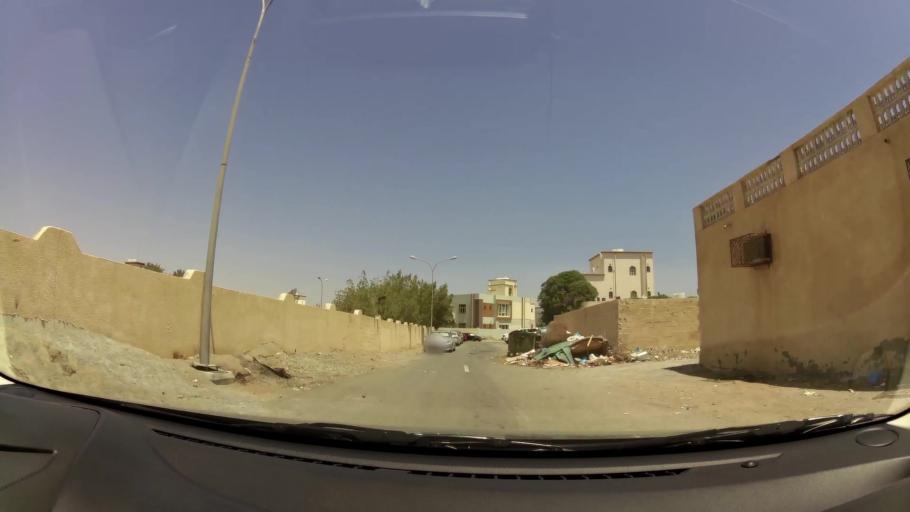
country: OM
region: Muhafazat Masqat
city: As Sib al Jadidah
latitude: 23.6267
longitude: 58.2401
